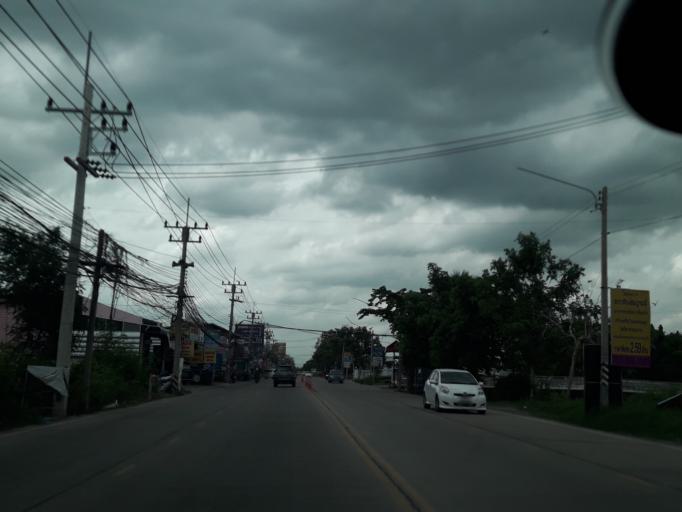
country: TH
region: Pathum Thani
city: Khlong Luang
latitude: 14.0571
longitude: 100.6635
